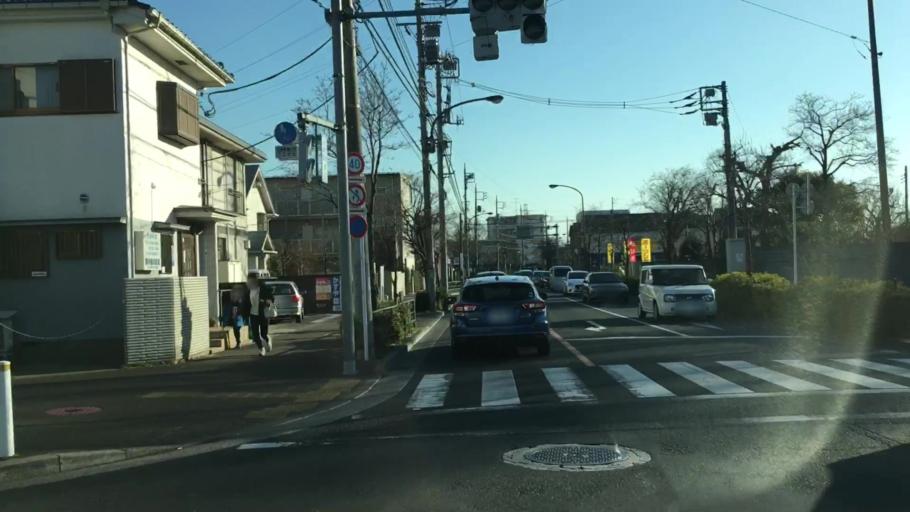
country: JP
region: Tokyo
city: Kamirenjaku
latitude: 35.6952
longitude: 139.5379
